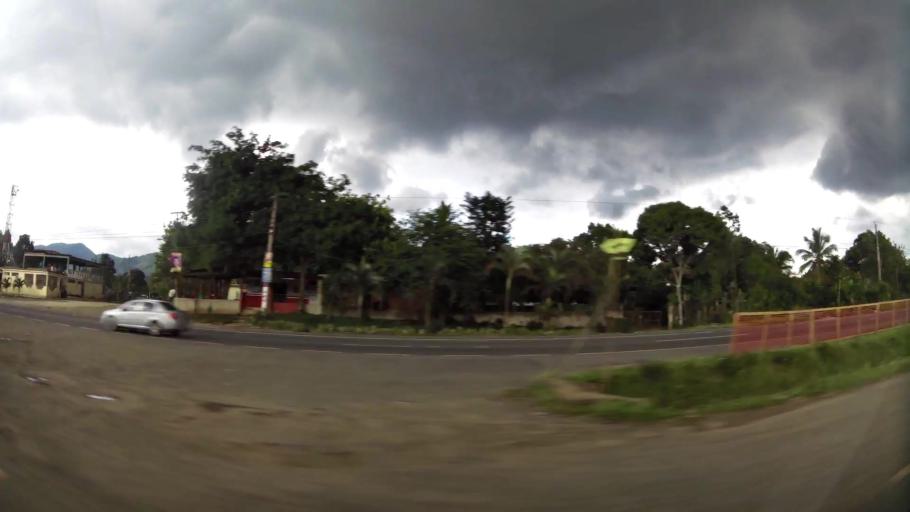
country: DO
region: San Cristobal
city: Villa Altagracia
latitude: 18.7508
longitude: -70.2340
